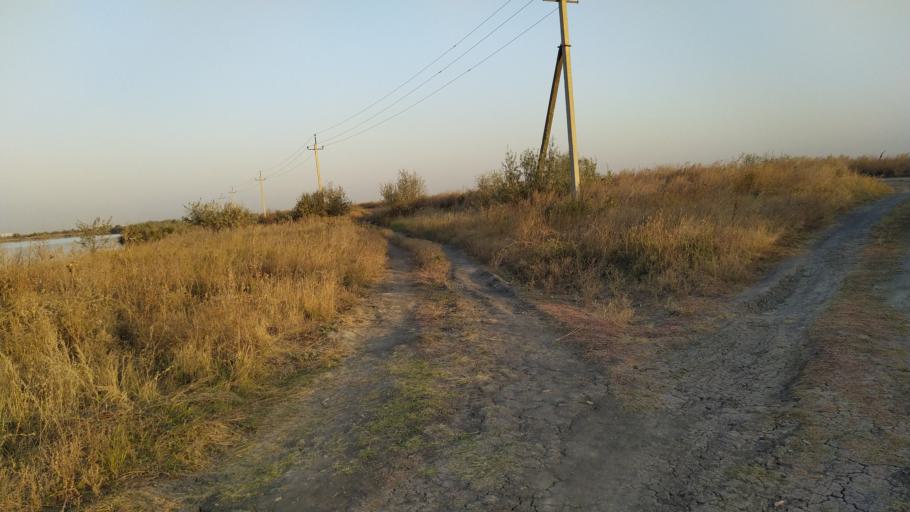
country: RU
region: Rostov
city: Bataysk
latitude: 47.1382
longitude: 39.6460
